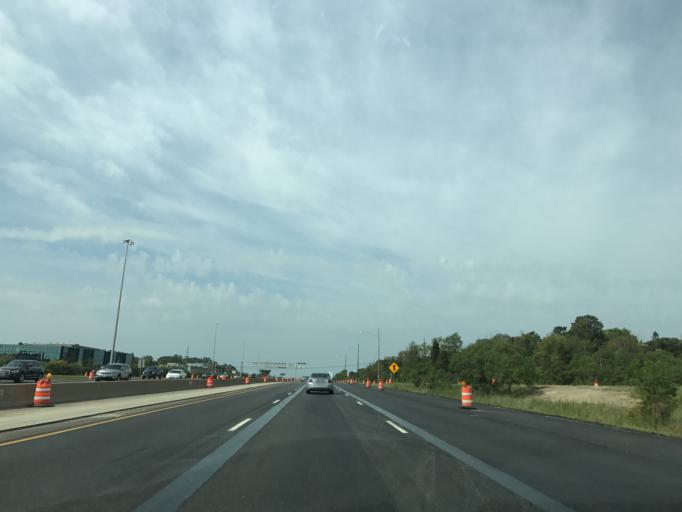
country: US
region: Illinois
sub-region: DuPage County
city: Burr Ridge
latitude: 41.7561
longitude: -87.9176
